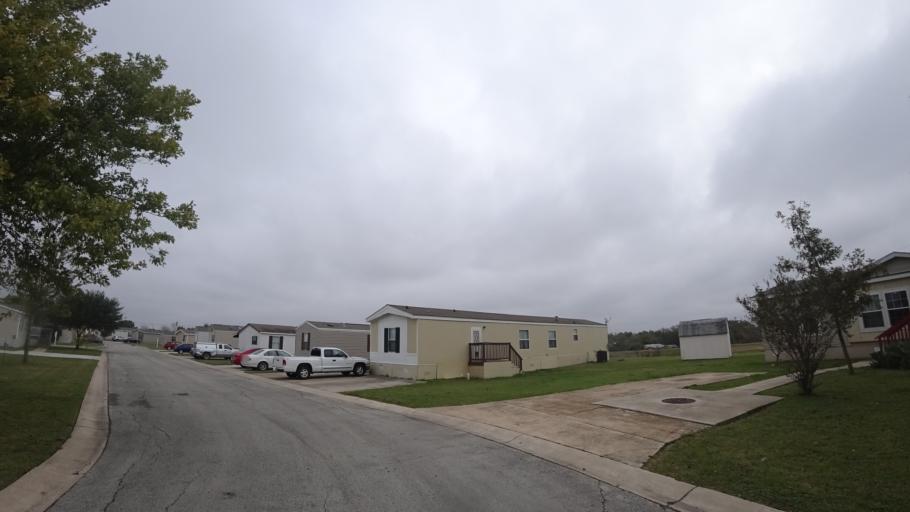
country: US
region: Texas
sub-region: Travis County
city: Pflugerville
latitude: 30.4095
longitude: -97.6054
